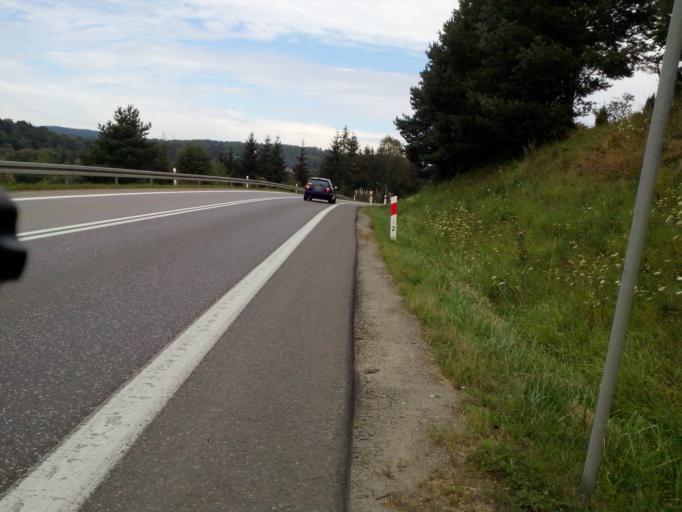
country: PL
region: Subcarpathian Voivodeship
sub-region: Powiat brzozowski
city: Jasienica Rosielna
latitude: 49.7672
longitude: 21.9558
